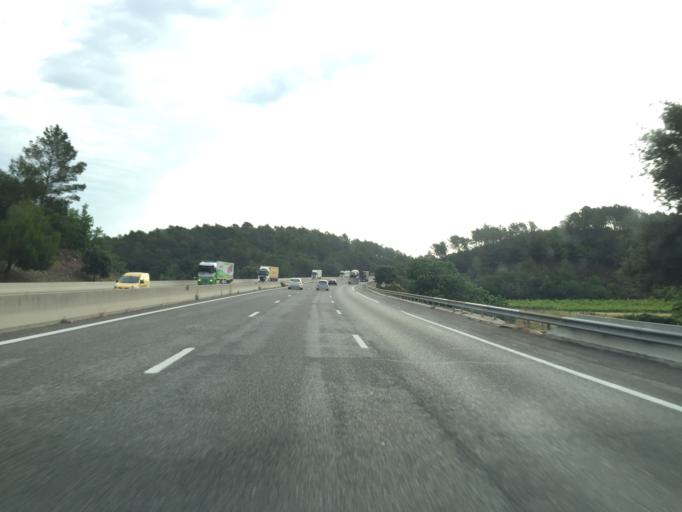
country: FR
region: Provence-Alpes-Cote d'Azur
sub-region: Departement du Var
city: Cabasse
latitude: 43.4022
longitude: 6.2323
